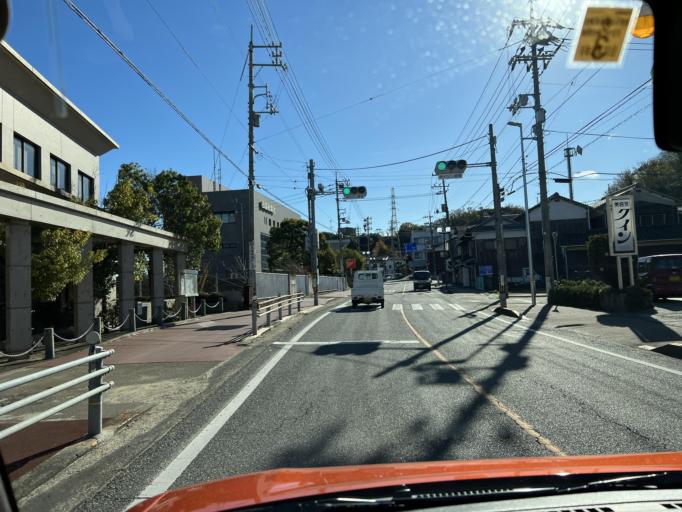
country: JP
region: Kagawa
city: Tonosho
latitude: 34.4858
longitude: 134.1792
